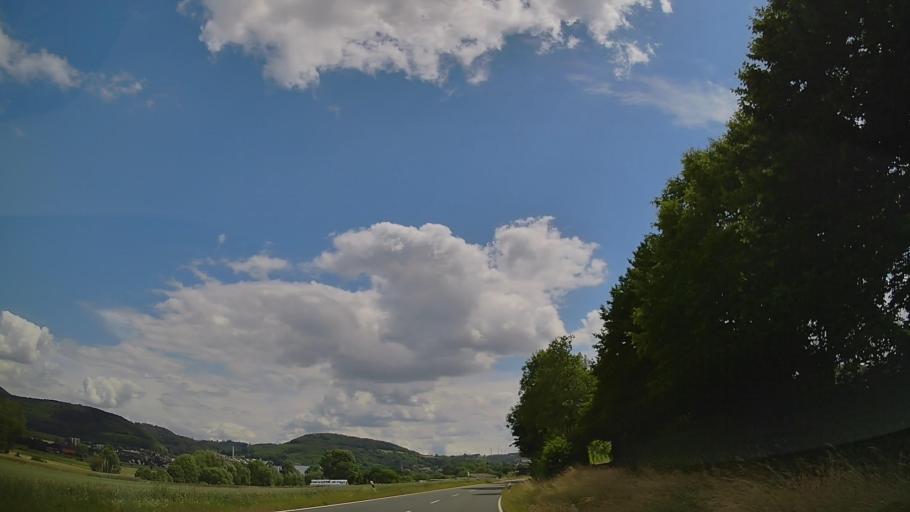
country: DE
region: North Rhine-Westphalia
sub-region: Regierungsbezirk Detmold
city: Lugde
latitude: 51.9709
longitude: 9.2348
